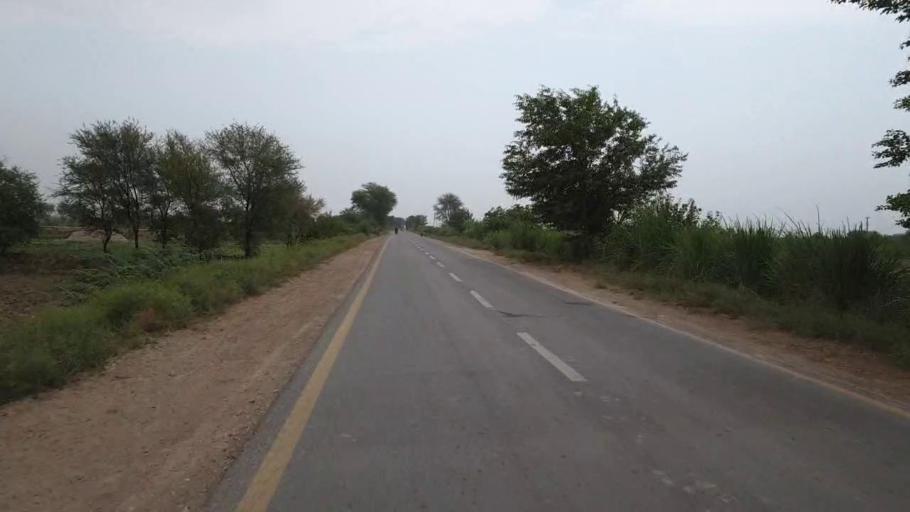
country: PK
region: Sindh
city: Bandhi
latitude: 26.5895
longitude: 68.2127
